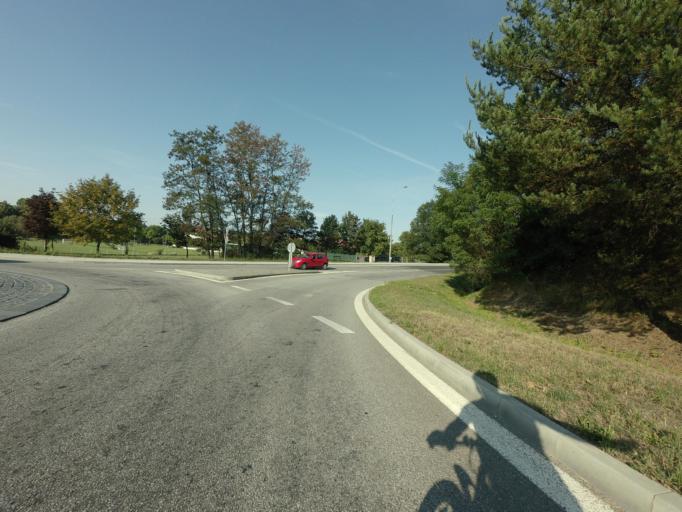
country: CZ
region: Jihocesky
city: Tyn nad Vltavou
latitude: 49.2283
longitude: 14.4243
